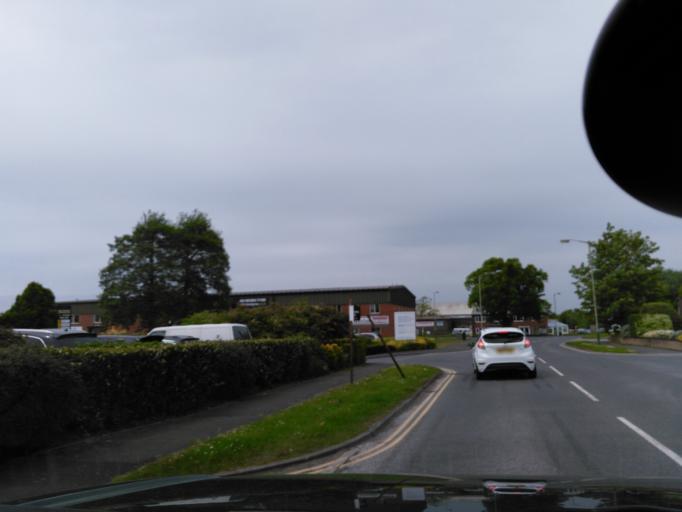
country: GB
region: England
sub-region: Wiltshire
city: Melksham
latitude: 51.3602
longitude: -2.1293
